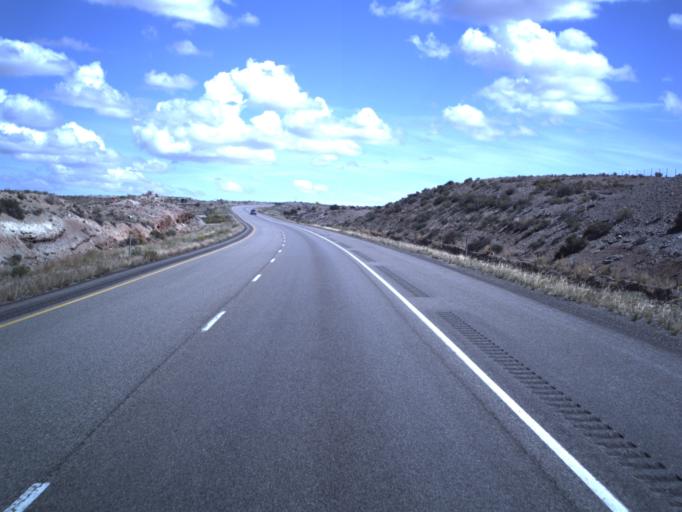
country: US
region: Utah
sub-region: Emery County
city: Ferron
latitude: 38.8437
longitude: -110.9826
